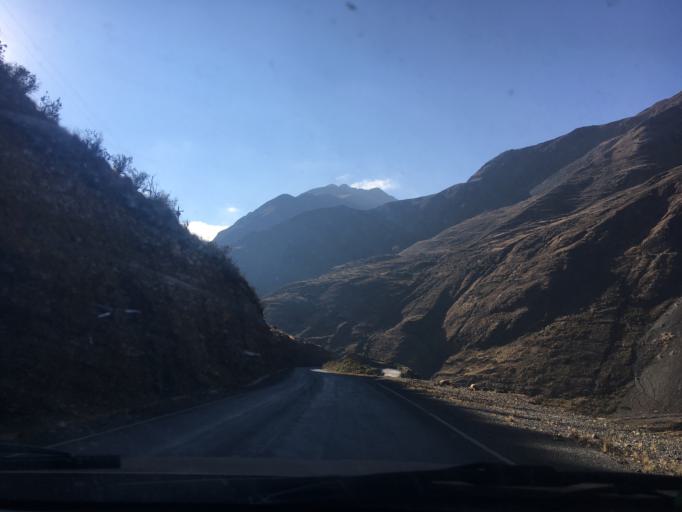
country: BO
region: La Paz
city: Quime
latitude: -17.0022
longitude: -67.2709
